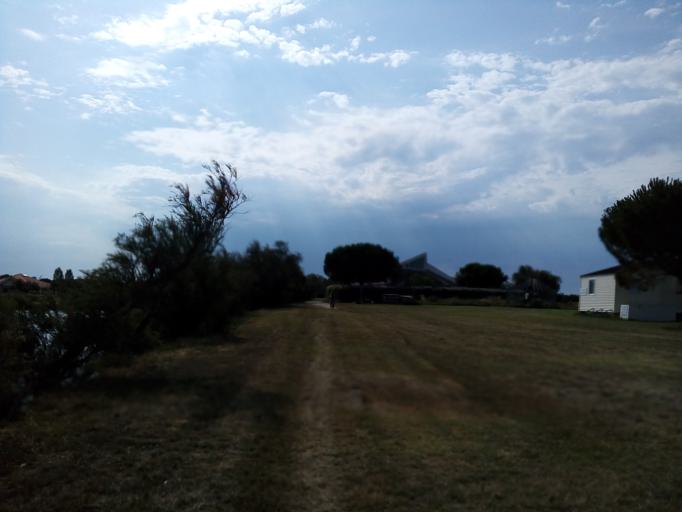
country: FR
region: Poitou-Charentes
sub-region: Departement de la Charente-Maritime
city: Boyard-Ville
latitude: 45.9520
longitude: -1.2446
